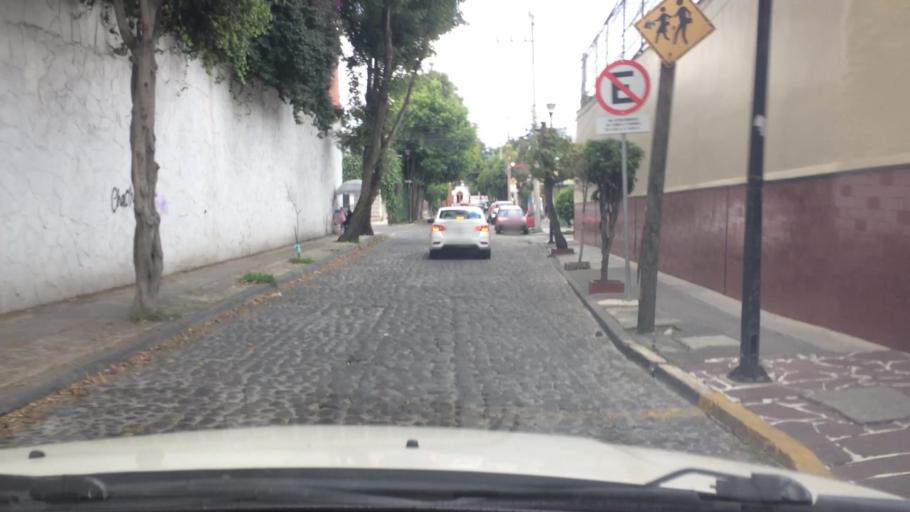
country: MX
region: Mexico City
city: Alvaro Obregon
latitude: 19.3552
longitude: -99.1946
